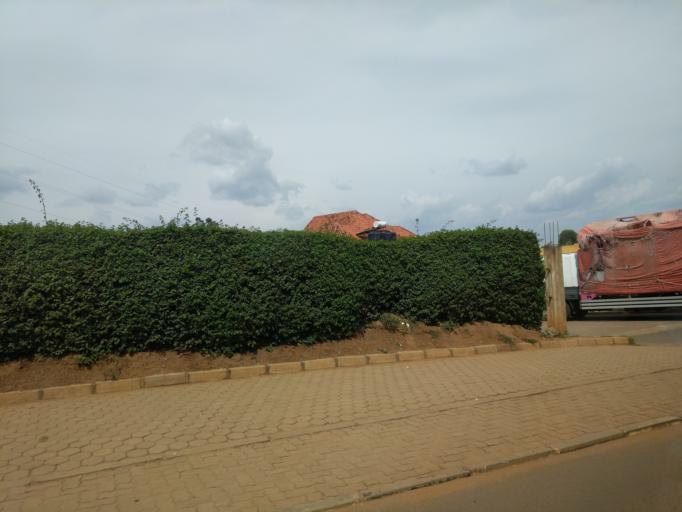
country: RW
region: Kigali
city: Kigali
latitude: -1.9821
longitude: 30.1178
